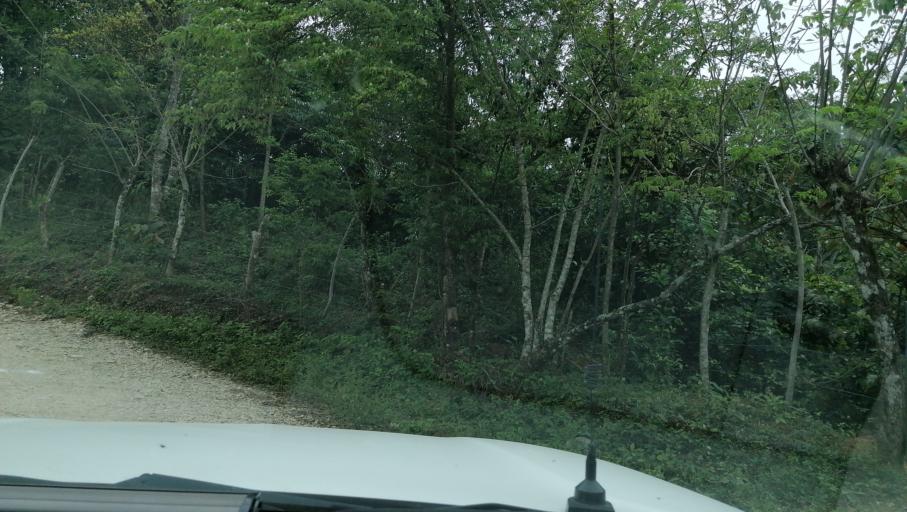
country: MX
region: Chiapas
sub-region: Ocotepec
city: San Pablo Huacano
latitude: 17.2734
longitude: -93.2431
